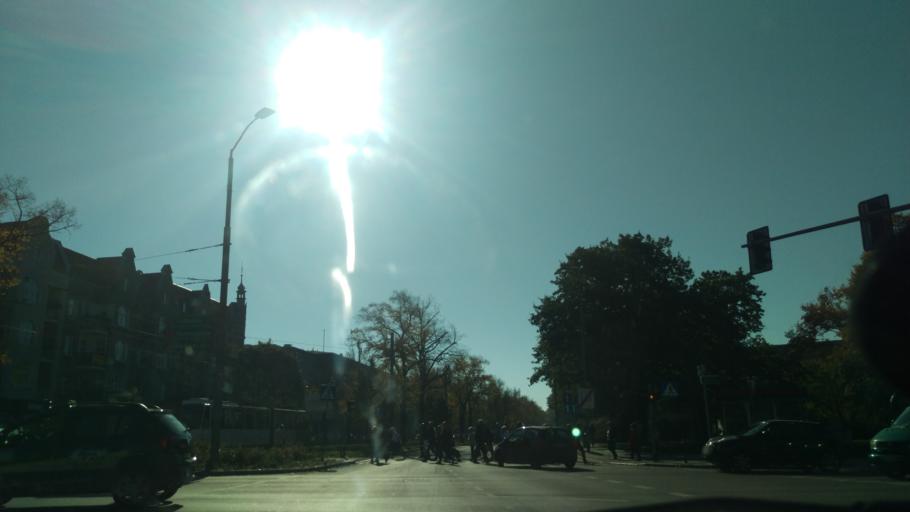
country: PL
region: West Pomeranian Voivodeship
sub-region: Szczecin
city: Szczecin
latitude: 53.4271
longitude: 14.5368
